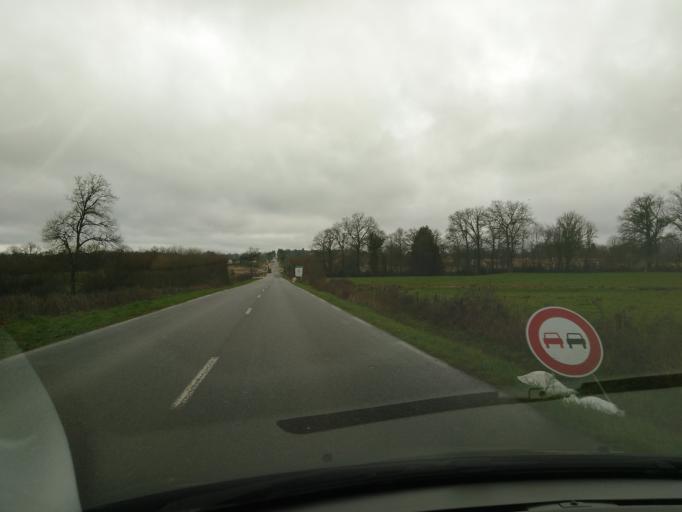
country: FR
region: Limousin
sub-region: Departement de la Haute-Vienne
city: Solignac
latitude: 45.7107
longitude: 1.2441
